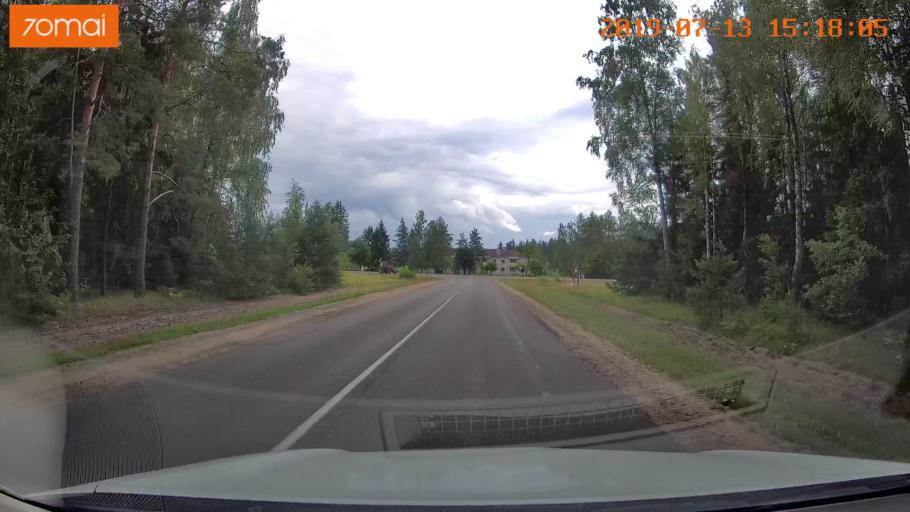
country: BY
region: Mogilev
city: Hlusha
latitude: 53.0878
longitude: 28.8463
